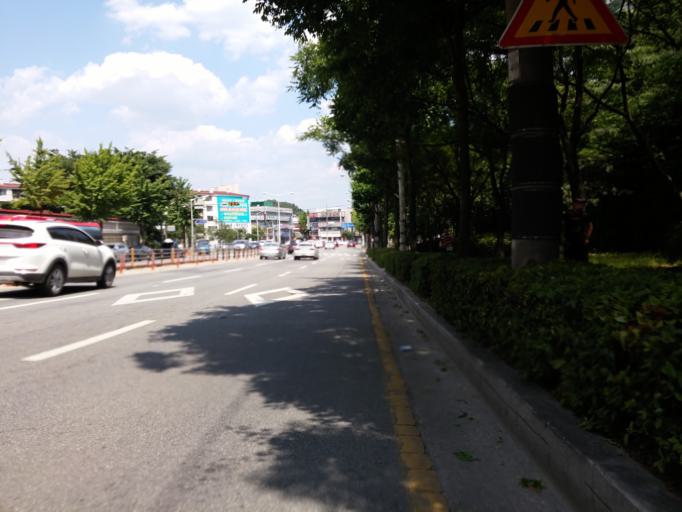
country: KR
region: Chungcheongbuk-do
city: Cheongju-si
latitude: 36.6281
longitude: 127.4388
